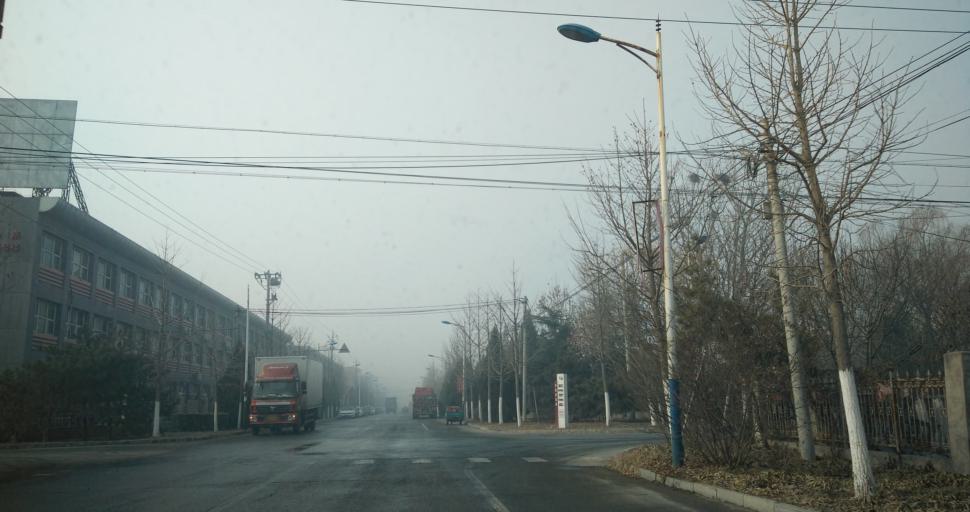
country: CN
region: Beijing
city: Yinghai
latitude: 39.7469
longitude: 116.4464
